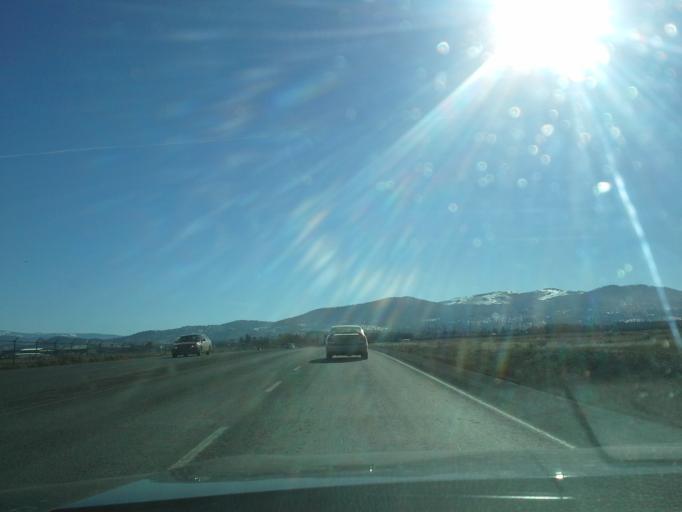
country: US
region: Montana
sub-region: Lewis and Clark County
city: Helena
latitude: 46.6119
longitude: -112.0049
